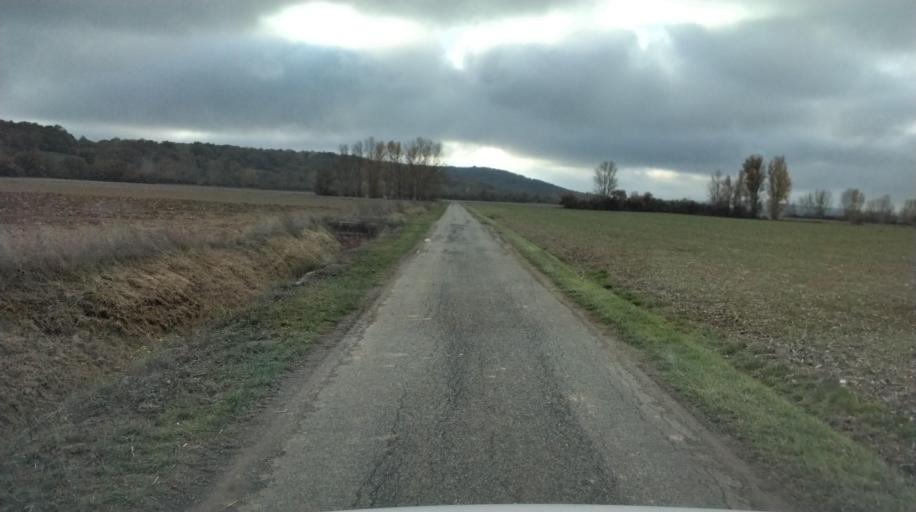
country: FR
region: Midi-Pyrenees
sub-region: Departement de la Haute-Garonne
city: Le Fousseret
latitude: 43.2705
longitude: 1.0616
